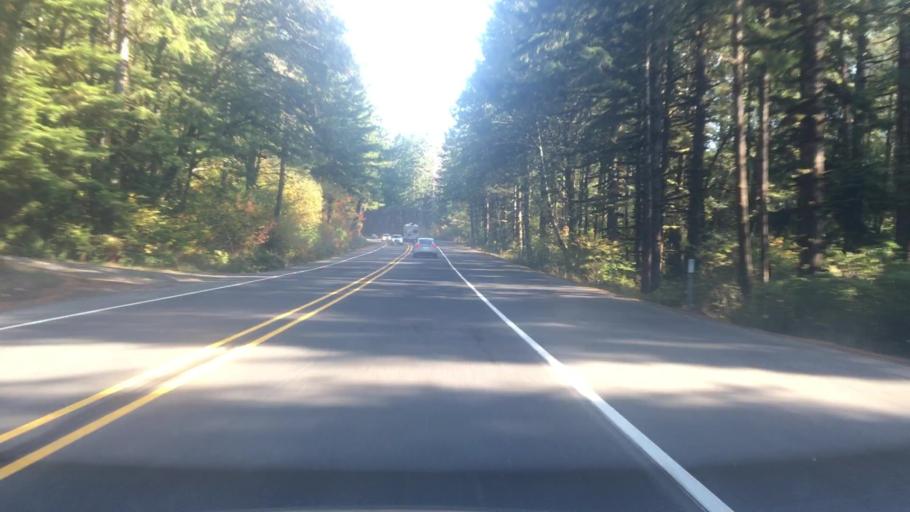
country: US
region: Oregon
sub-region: Lincoln County
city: Rose Lodge
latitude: 45.0558
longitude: -123.7521
